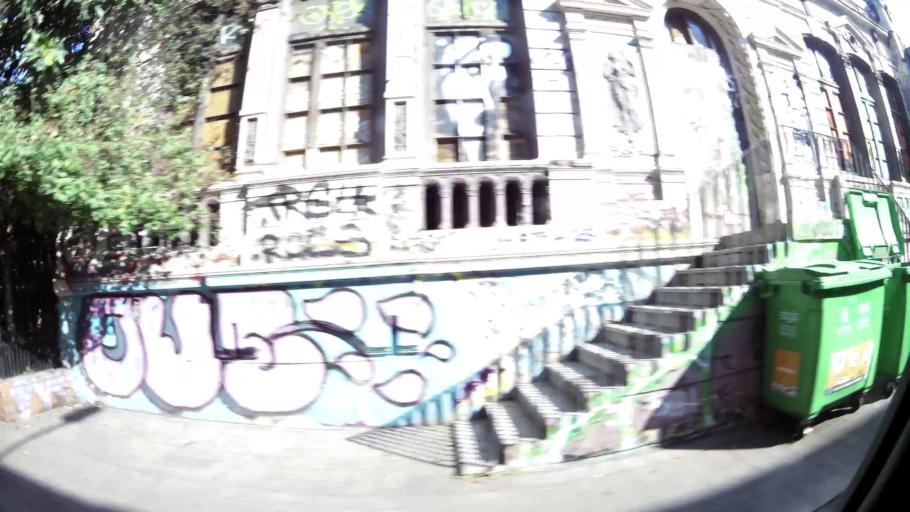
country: CL
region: Santiago Metropolitan
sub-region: Provincia de Santiago
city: Santiago
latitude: -33.4389
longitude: -70.6655
